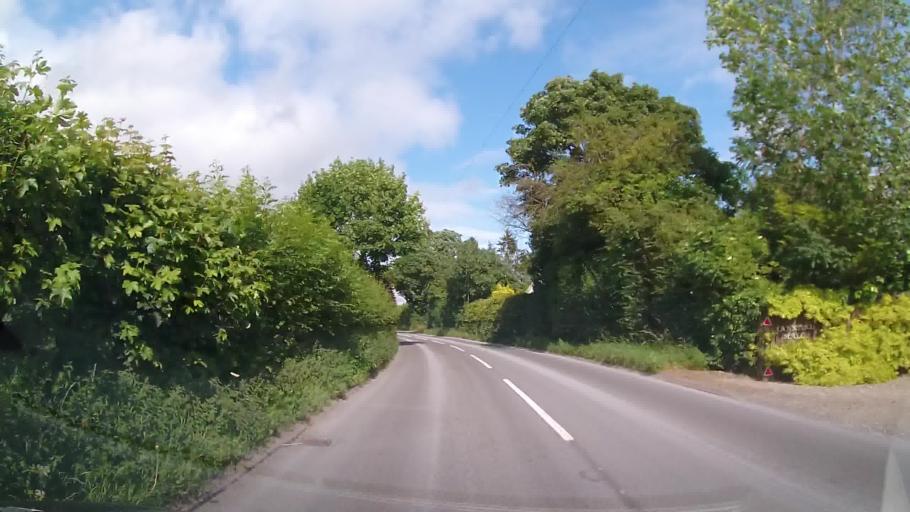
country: GB
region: England
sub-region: Shropshire
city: Pant
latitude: 52.8092
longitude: -3.0510
